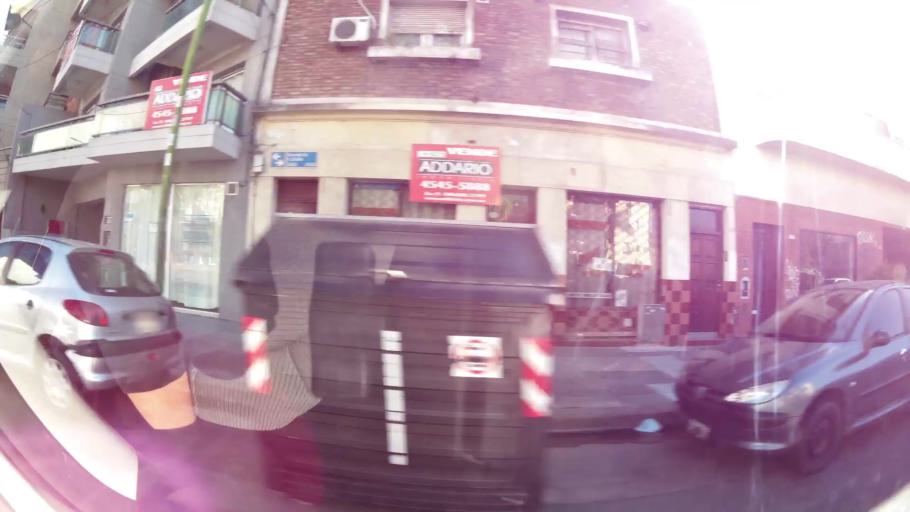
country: AR
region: Buenos Aires F.D.
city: Colegiales
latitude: -34.5564
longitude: -58.4800
